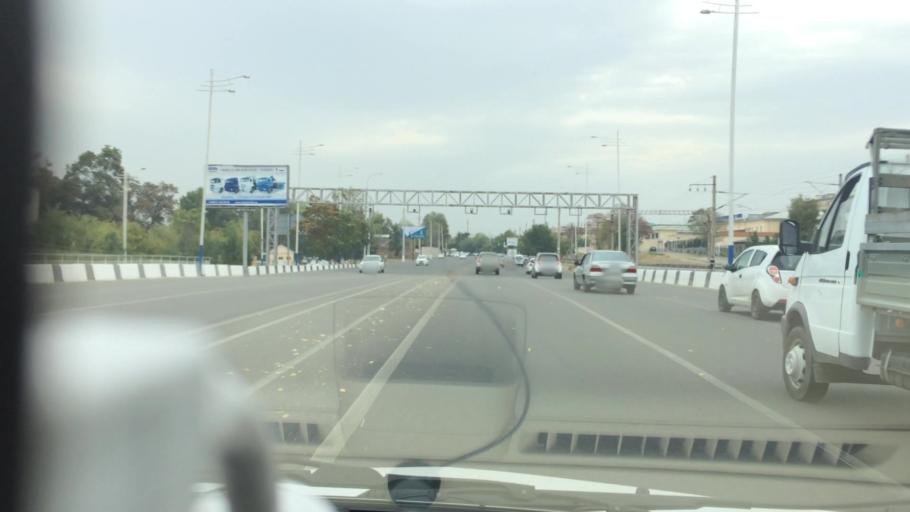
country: UZ
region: Toshkent Shahri
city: Tashkent
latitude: 41.3073
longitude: 69.3014
